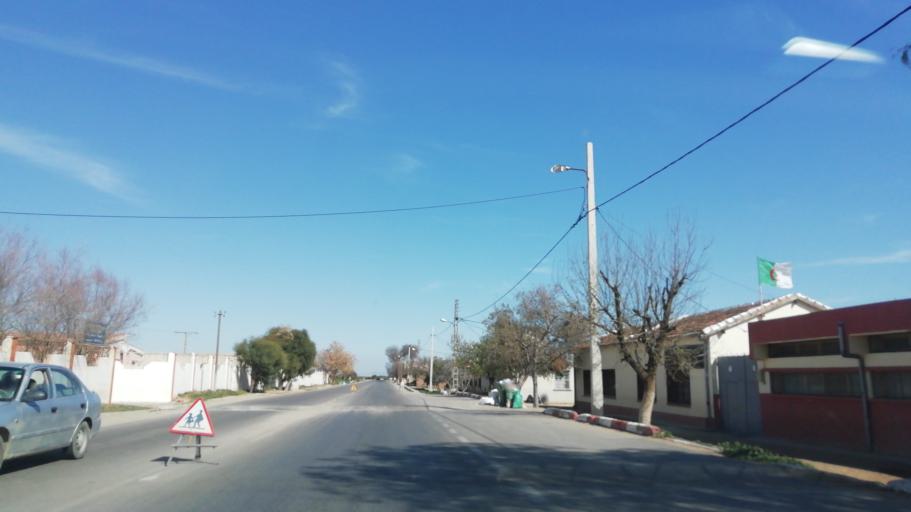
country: DZ
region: Mascara
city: Oued el Abtal
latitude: 35.4239
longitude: 0.4493
